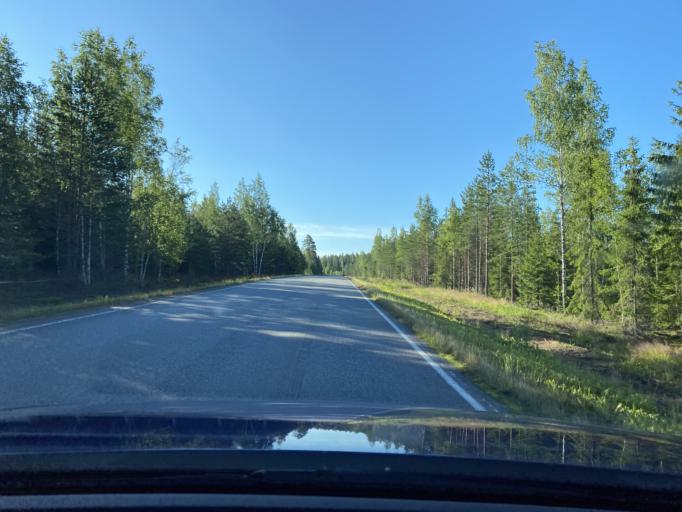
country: FI
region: Haeme
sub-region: Forssa
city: Tammela
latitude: 60.9184
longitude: 23.8362
